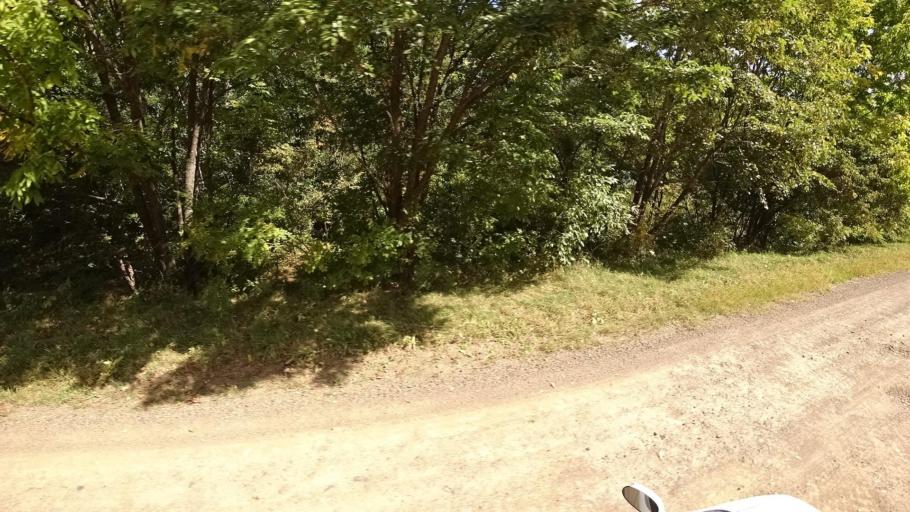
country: RU
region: Primorskiy
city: Yakovlevka
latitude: 44.7014
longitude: 133.6516
